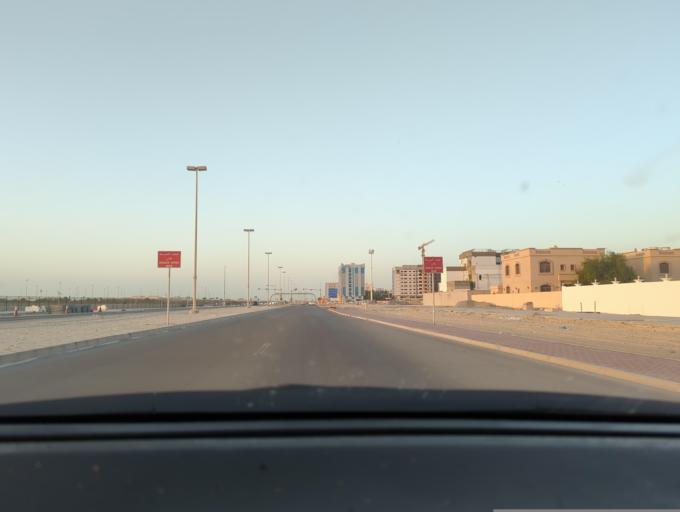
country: AE
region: Abu Dhabi
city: Abu Dhabi
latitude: 24.3124
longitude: 54.5307
